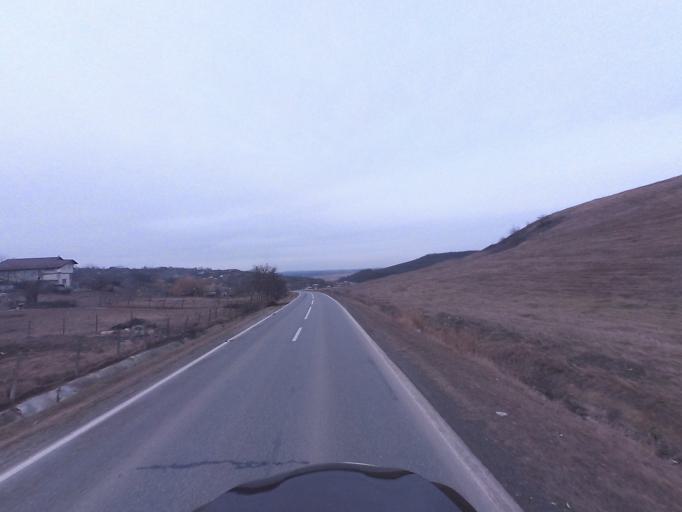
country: RO
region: Iasi
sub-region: Comuna Popricani
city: Popricani
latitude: 47.2927
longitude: 27.5110
